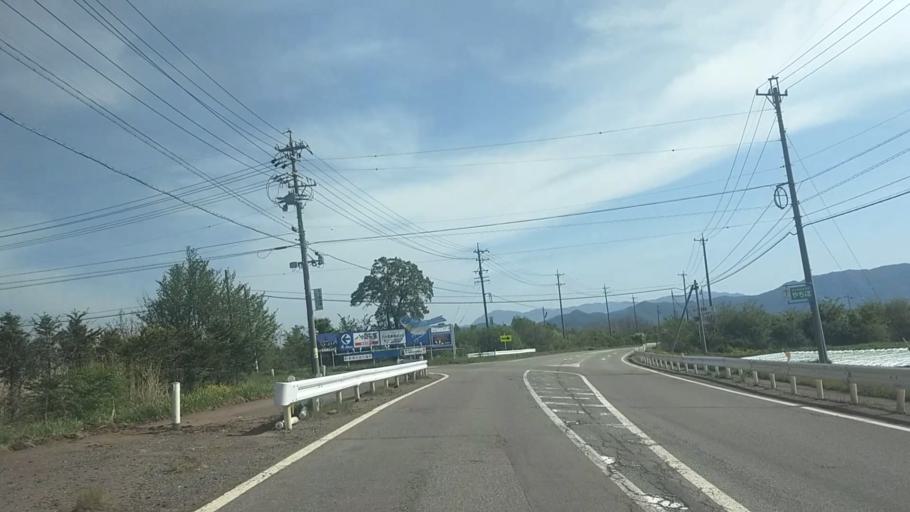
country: JP
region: Nagano
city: Saku
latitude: 35.9860
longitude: 138.4856
